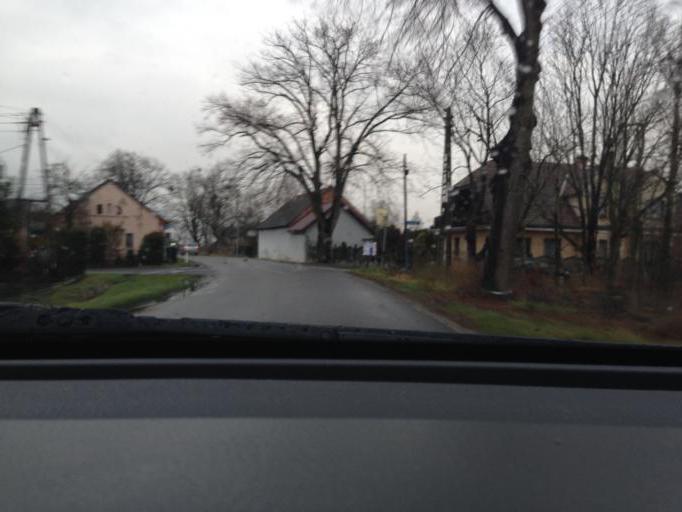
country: PL
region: Opole Voivodeship
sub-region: Powiat opolski
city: Wegry
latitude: 50.7304
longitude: 18.0482
